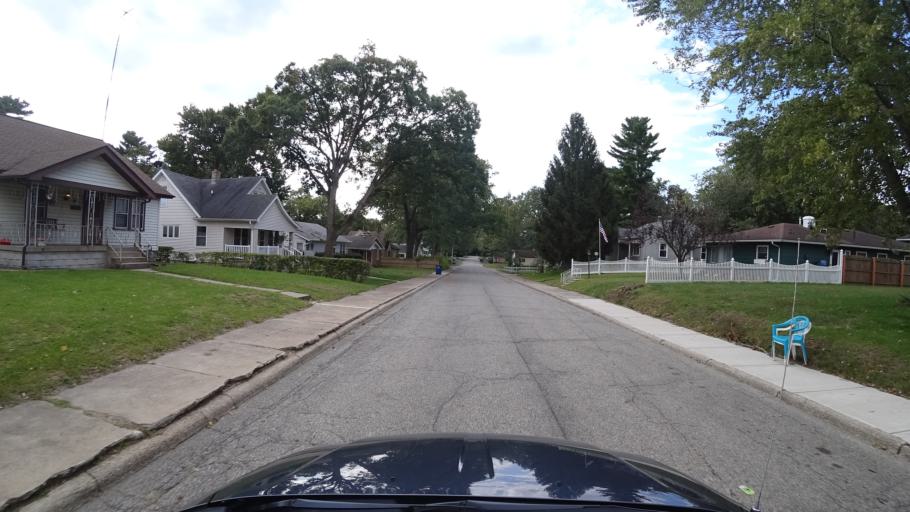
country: US
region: Indiana
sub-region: LaPorte County
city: Michigan City
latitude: 41.7067
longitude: -86.8772
